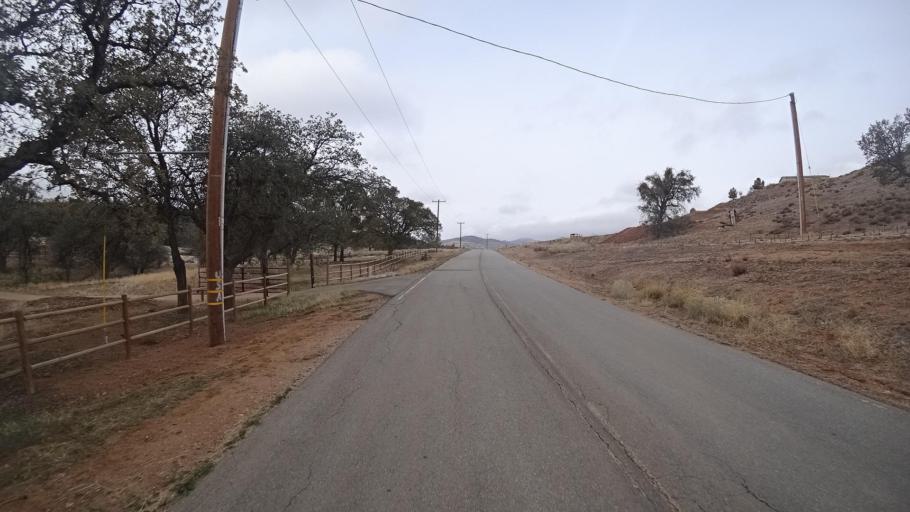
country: US
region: California
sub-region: Kern County
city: Tehachapi
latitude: 35.1740
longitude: -118.3636
